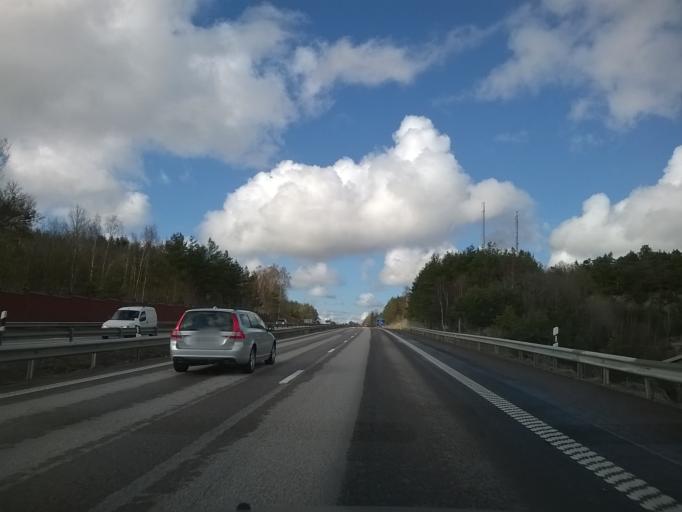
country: SE
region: Halland
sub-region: Kungsbacka Kommun
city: Fjaeras kyrkby
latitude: 57.4226
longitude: 12.1655
